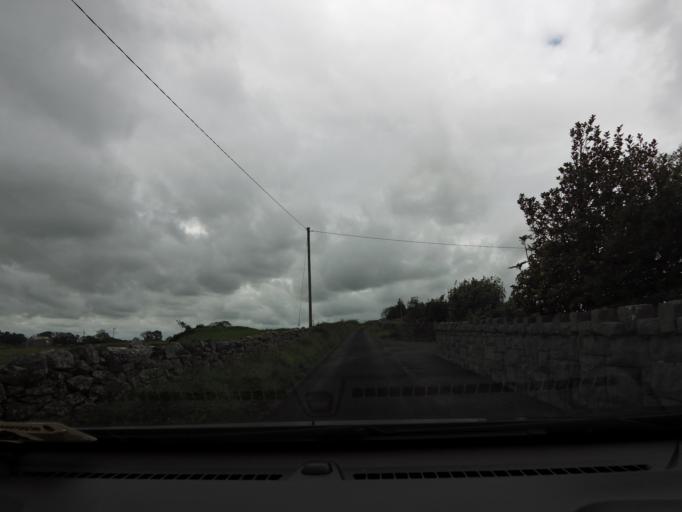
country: IE
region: Connaught
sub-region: County Galway
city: Athenry
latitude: 53.3108
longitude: -8.7433
